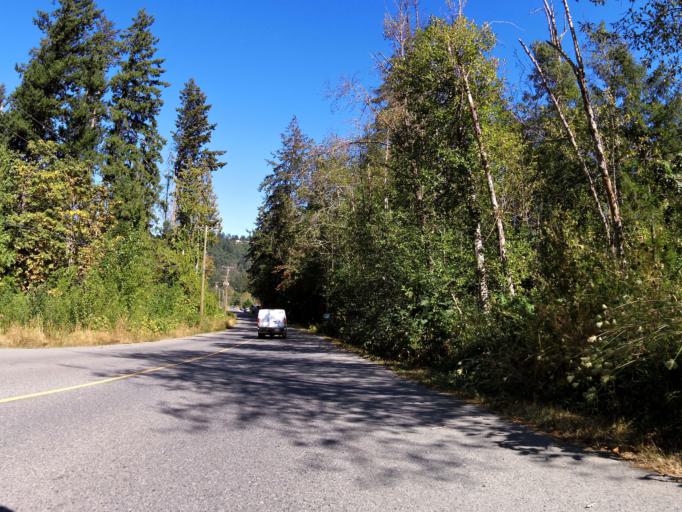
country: CA
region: British Columbia
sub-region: Cowichan Valley Regional District
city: Ladysmith
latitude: 49.0271
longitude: -123.8593
